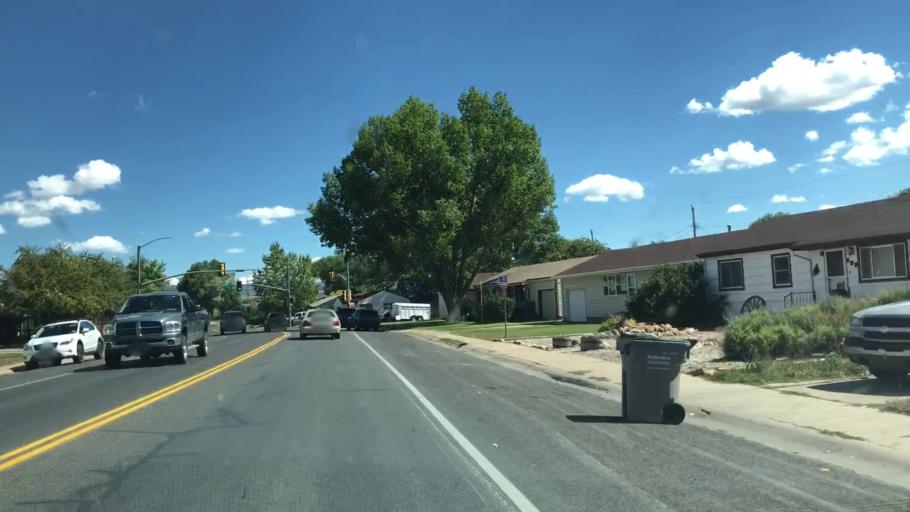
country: US
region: Wyoming
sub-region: Albany County
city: Laramie
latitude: 41.3255
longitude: -105.5853
